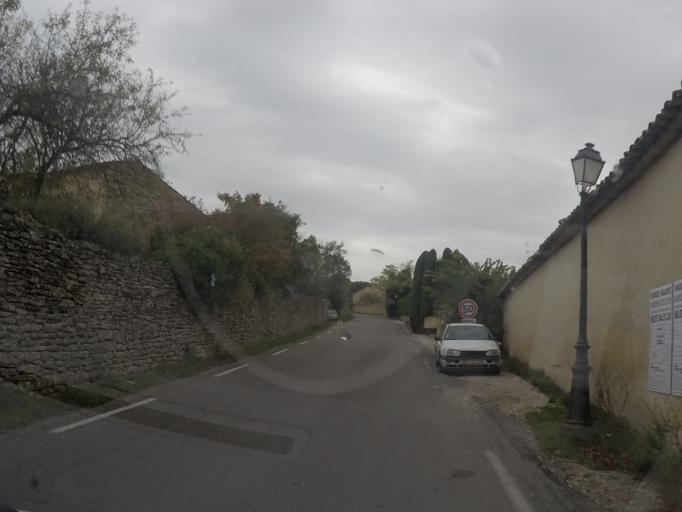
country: FR
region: Provence-Alpes-Cote d'Azur
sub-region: Departement du Vaucluse
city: Gordes
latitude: 43.9126
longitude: 5.1963
